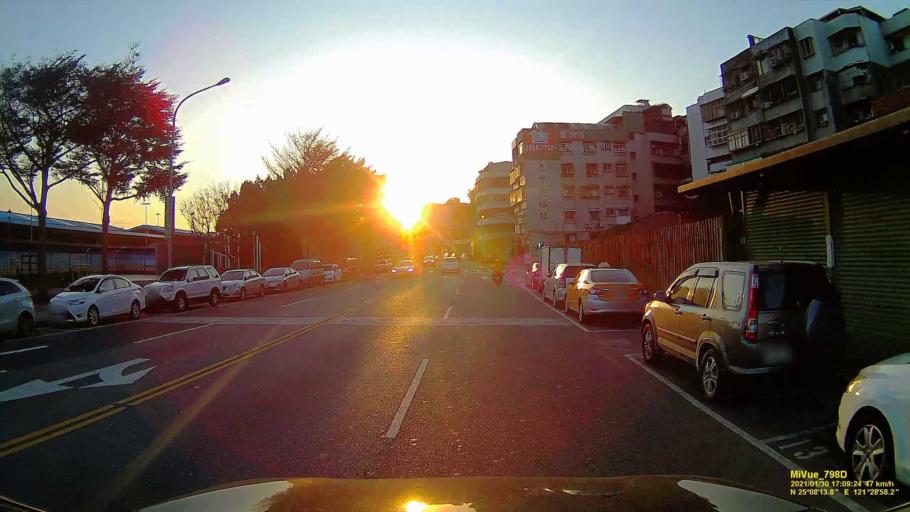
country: TW
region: Taipei
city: Taipei
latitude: 25.1371
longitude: 121.4826
